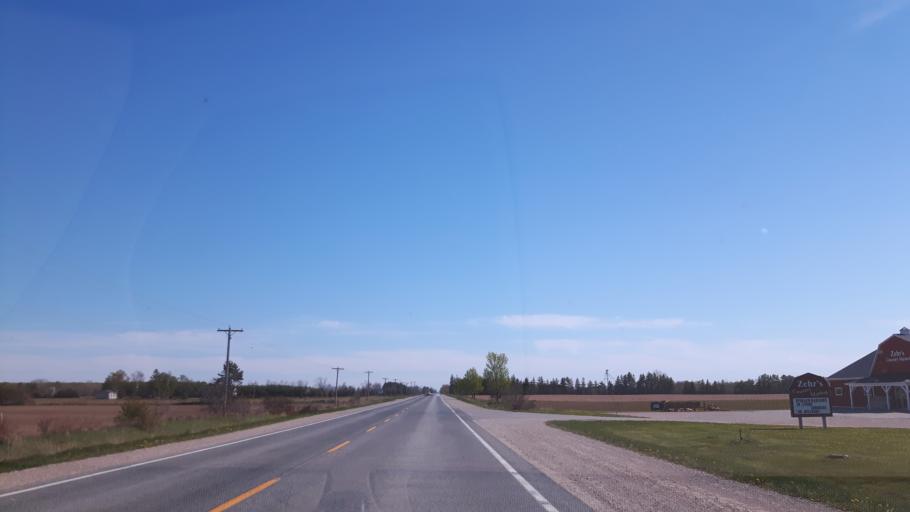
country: CA
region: Ontario
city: Bluewater
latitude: 43.5227
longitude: -81.6929
